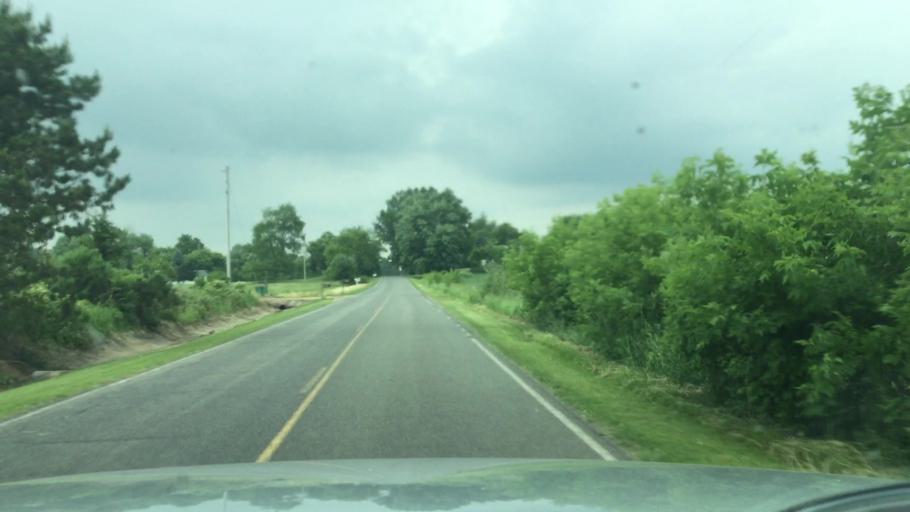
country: US
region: Michigan
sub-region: Shiawassee County
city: Durand
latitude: 42.7944
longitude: -84.0020
